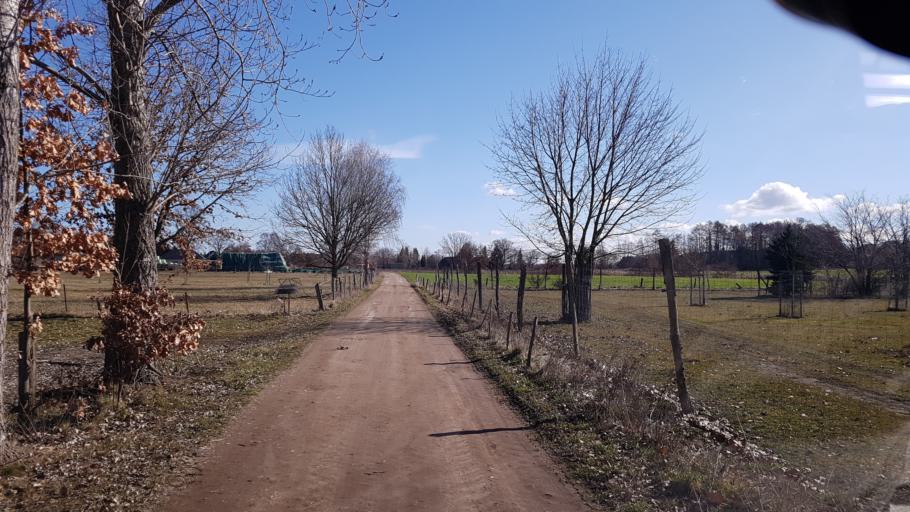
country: DE
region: Brandenburg
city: Schonborn
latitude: 51.5664
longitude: 13.5160
